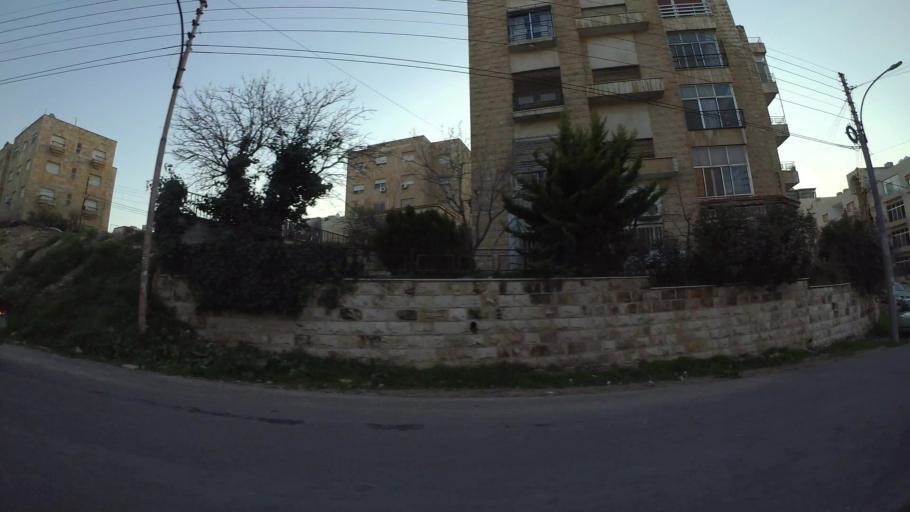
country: JO
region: Amman
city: Al Jubayhah
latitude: 31.9976
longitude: 35.8789
